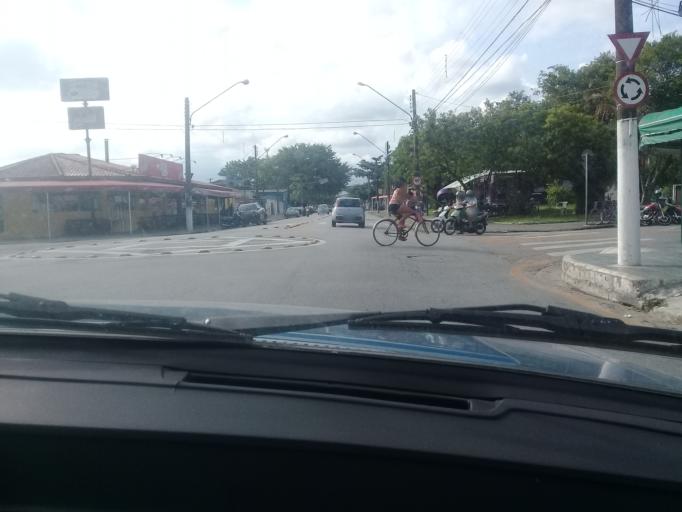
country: BR
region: Sao Paulo
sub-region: Guaruja
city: Guaruja
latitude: -23.9949
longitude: -46.2761
